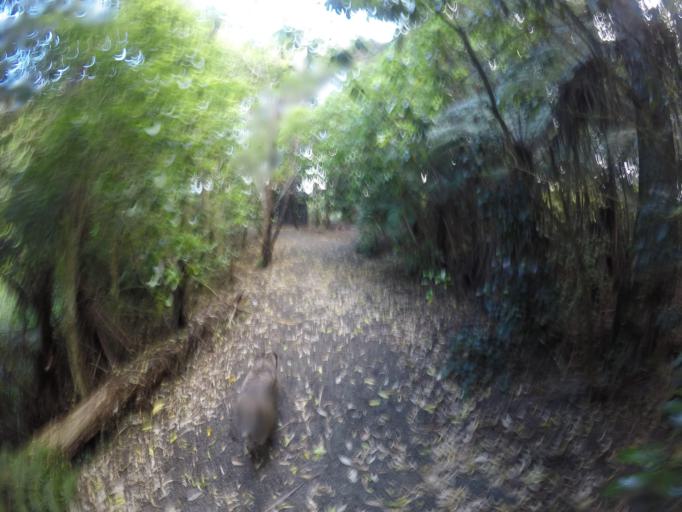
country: NZ
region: Auckland
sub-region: Auckland
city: Titirangi
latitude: -36.9304
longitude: 174.6510
